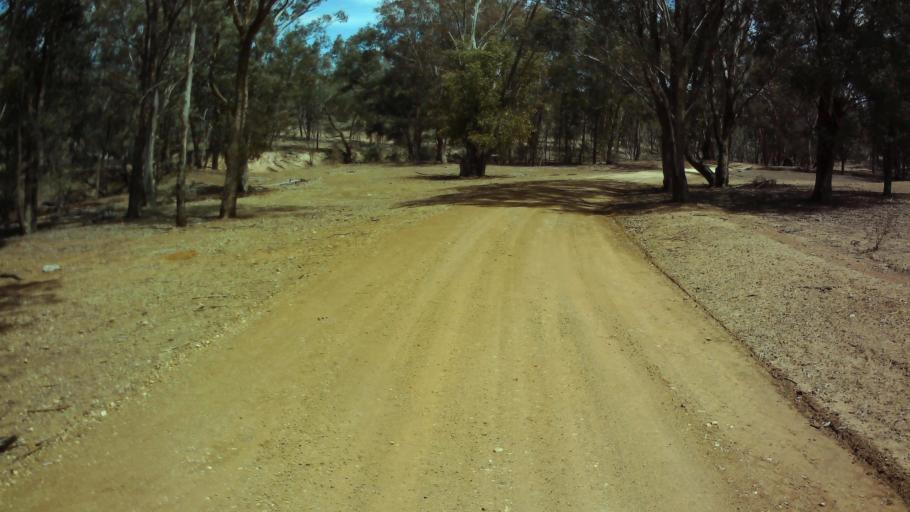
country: AU
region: New South Wales
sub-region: Weddin
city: Grenfell
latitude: -33.7980
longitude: 148.1603
